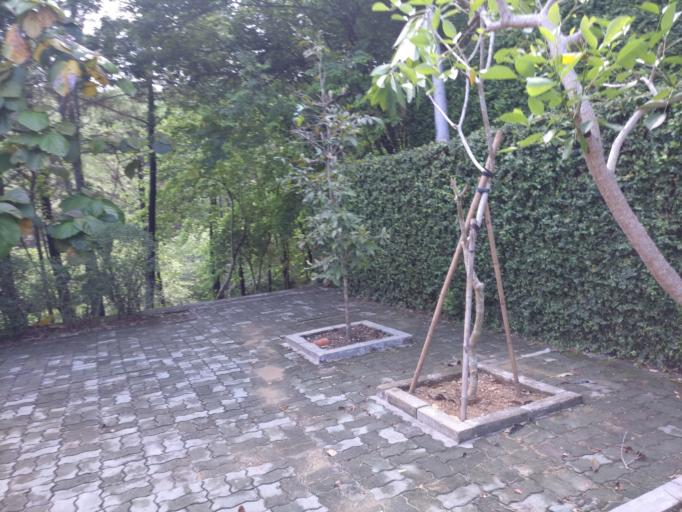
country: VN
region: Thua Thien-Hue
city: Hue
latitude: 16.4205
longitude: 107.6076
